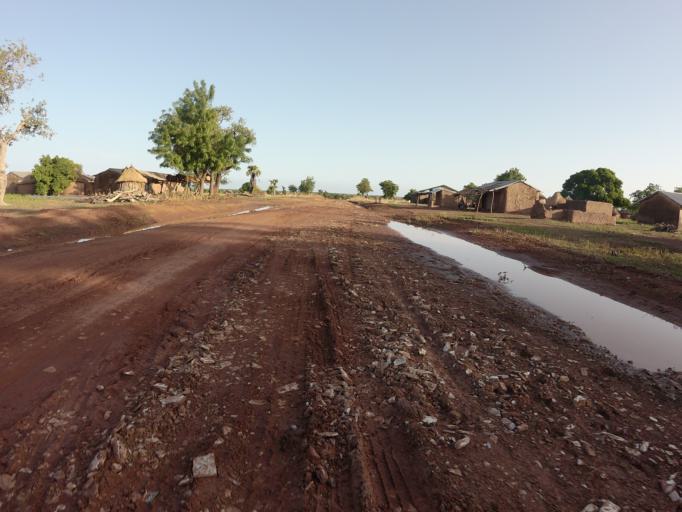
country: TG
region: Savanes
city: Sansanne-Mango
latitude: 10.3545
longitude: -0.0932
